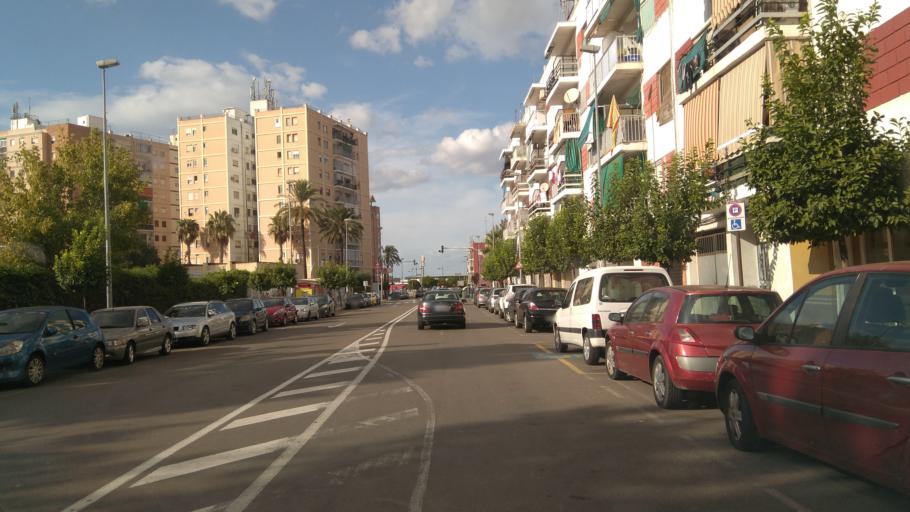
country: ES
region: Valencia
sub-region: Provincia de Valencia
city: Alzira
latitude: 39.1575
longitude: -0.4287
